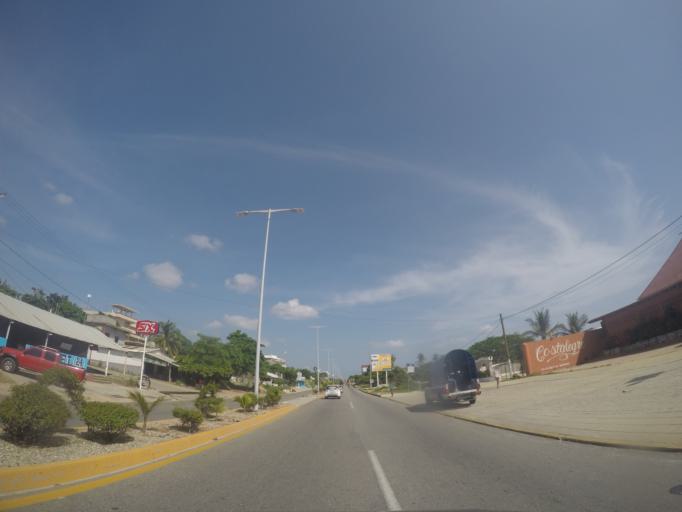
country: MX
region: Oaxaca
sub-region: Santa Maria Colotepec
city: Brisas de Zicatela
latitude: 15.8539
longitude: -97.0538
